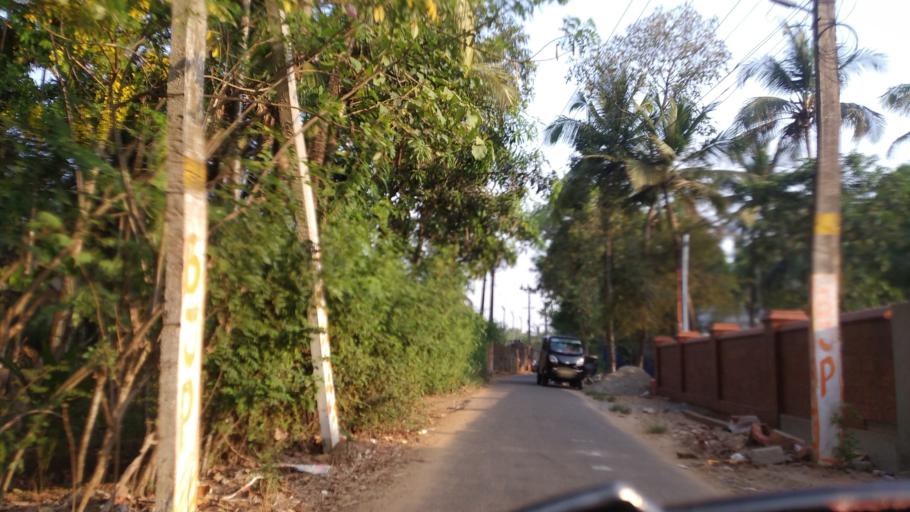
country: IN
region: Kerala
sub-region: Thrissur District
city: Thanniyam
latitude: 10.4261
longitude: 76.0814
